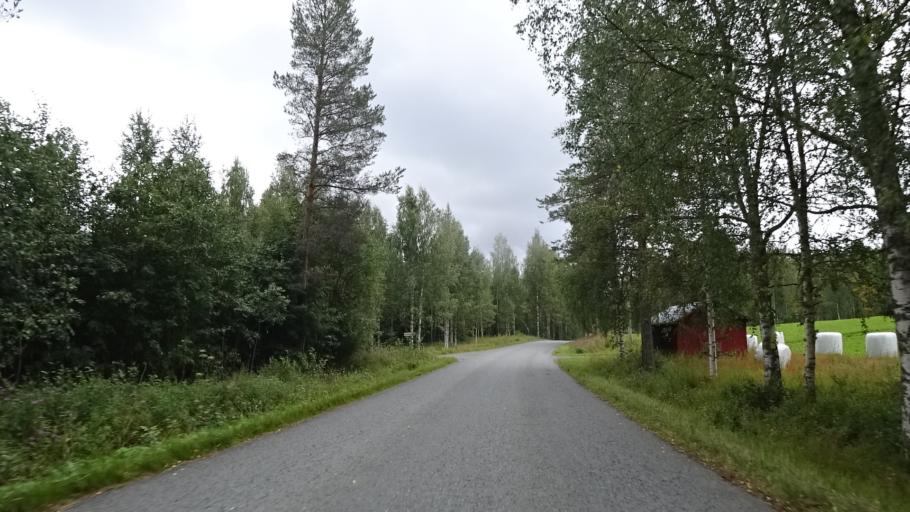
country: FI
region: North Karelia
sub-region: Joensuu
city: Ilomantsi
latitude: 62.9519
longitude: 31.2963
